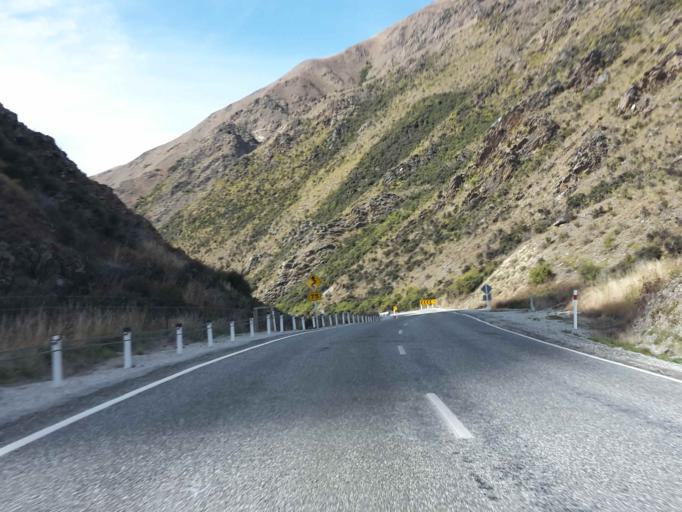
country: NZ
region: Otago
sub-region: Queenstown-Lakes District
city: Wanaka
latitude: -44.6001
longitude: 169.5629
